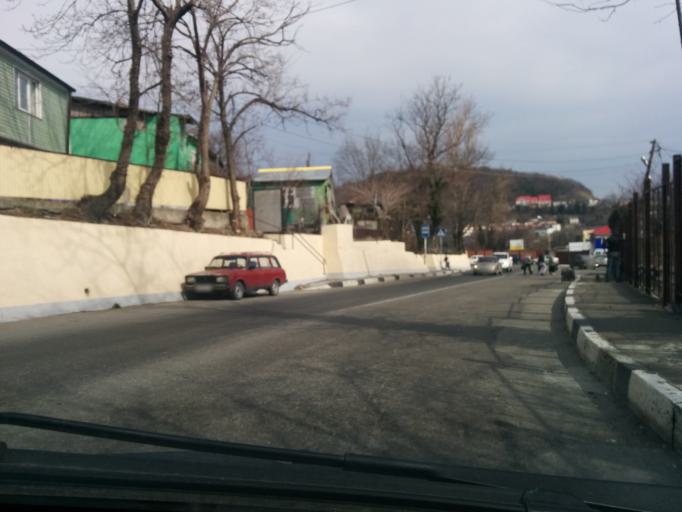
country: RU
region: Krasnodarskiy
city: Tuapse
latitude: 44.1013
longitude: 39.0657
